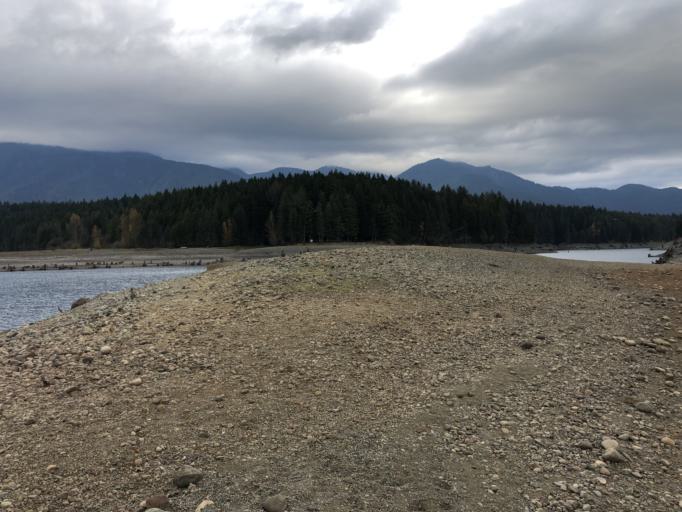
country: US
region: Washington
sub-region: Mason County
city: Shelton
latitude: 47.4628
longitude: -123.2243
